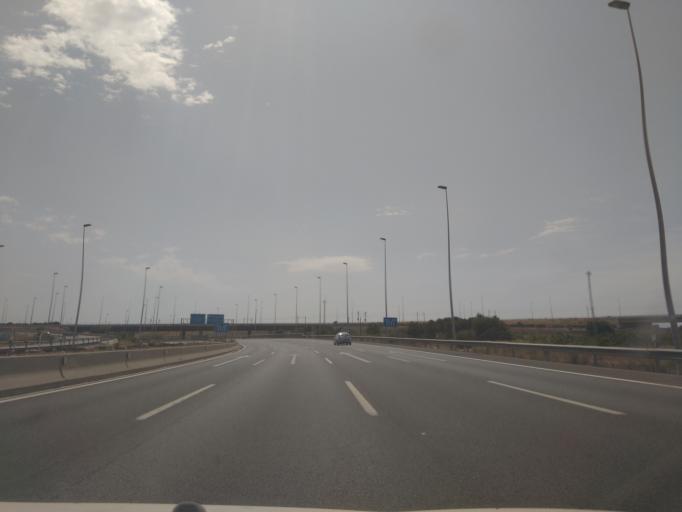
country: ES
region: Valencia
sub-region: Provincia de Valencia
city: Silla
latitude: 39.3514
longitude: -0.4277
